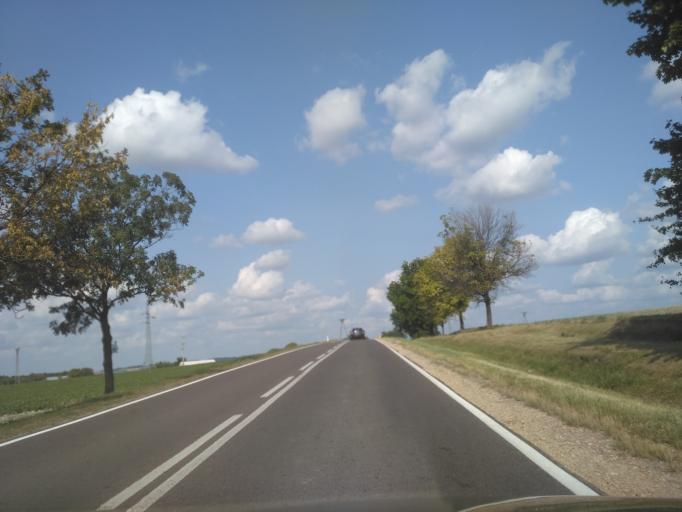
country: PL
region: Lublin Voivodeship
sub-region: Powiat chelmski
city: Rejowiec
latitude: 51.1071
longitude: 23.3118
